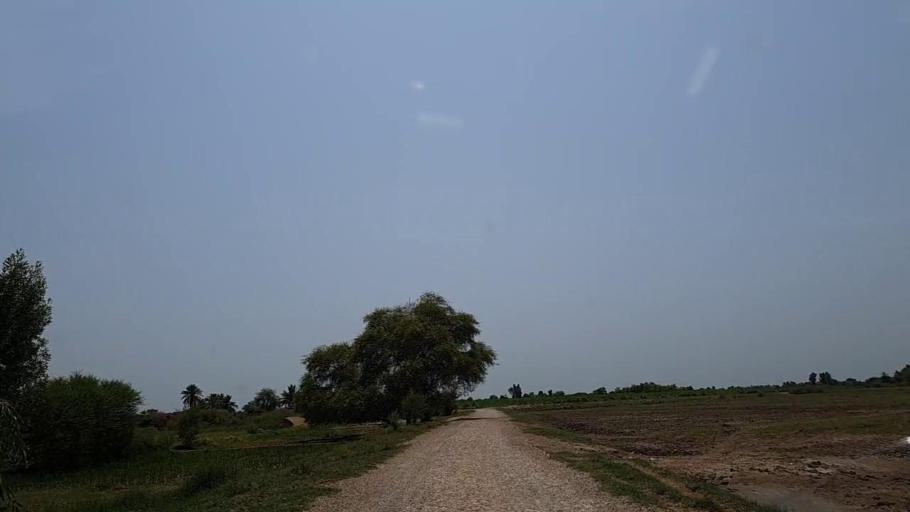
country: PK
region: Sindh
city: Ghotki
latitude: 27.9881
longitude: 69.4080
